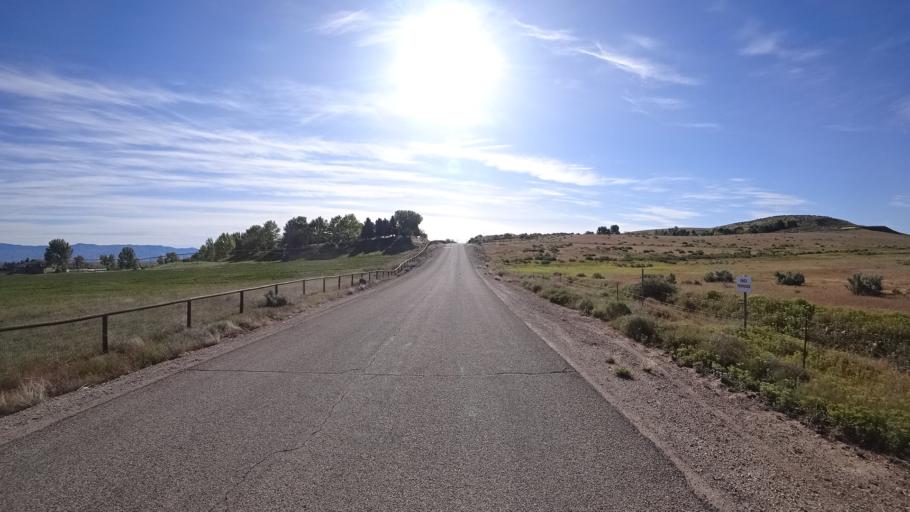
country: US
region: Idaho
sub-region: Ada County
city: Garden City
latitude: 43.5248
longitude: -116.2784
